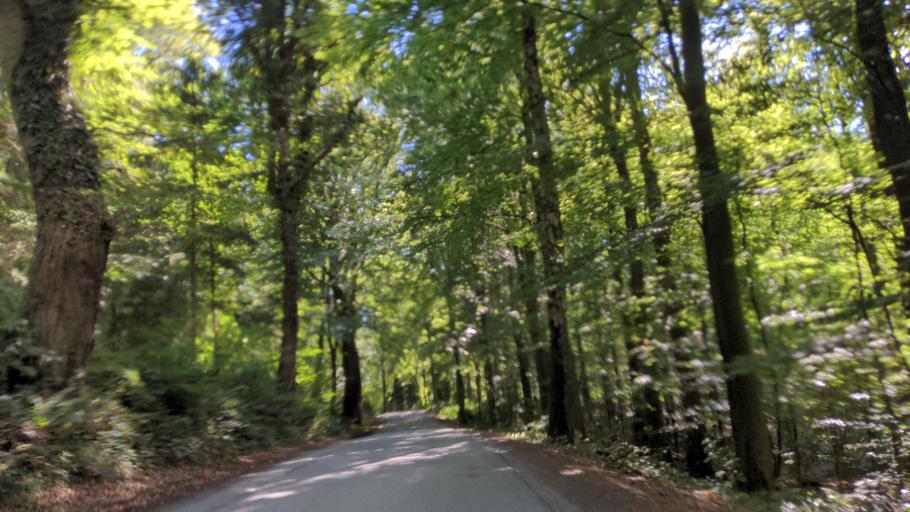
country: DE
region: Schleswig-Holstein
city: Kasseedorf
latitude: 54.1467
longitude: 10.7241
